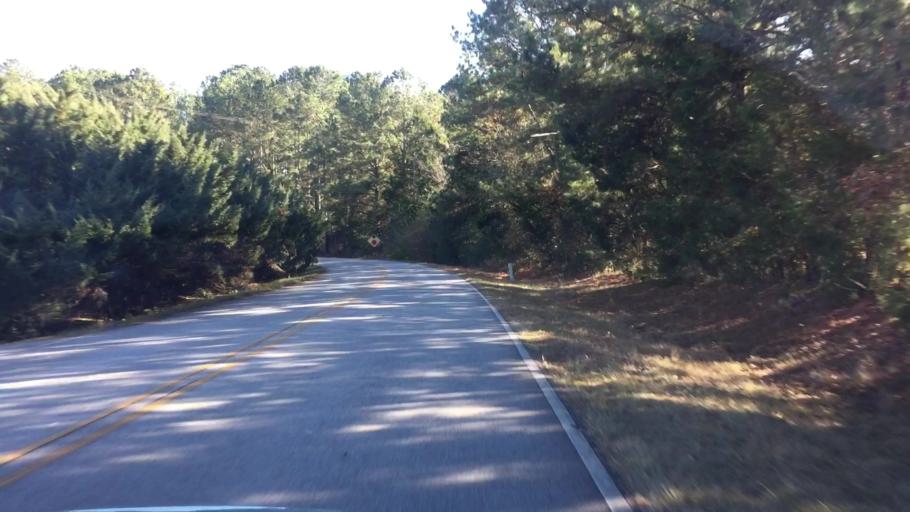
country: US
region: Georgia
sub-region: Newton County
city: Oakwood
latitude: 33.4764
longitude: -83.9649
